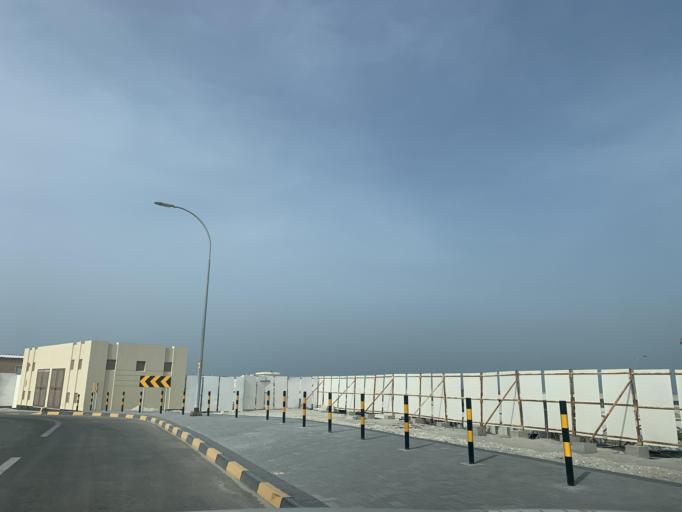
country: BH
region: Muharraq
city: Al Muharraq
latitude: 26.3224
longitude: 50.6311
